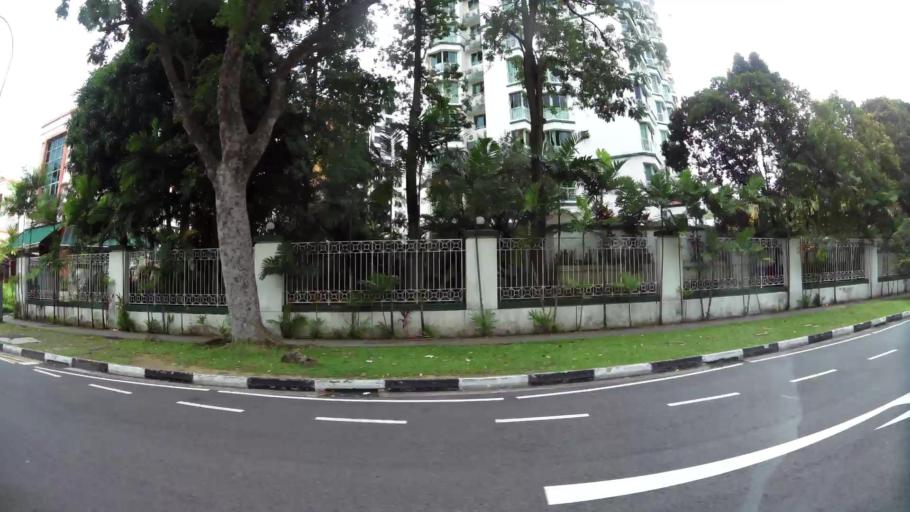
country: MY
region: Johor
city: Kampung Pasir Gudang Baru
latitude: 1.3802
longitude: 103.8877
